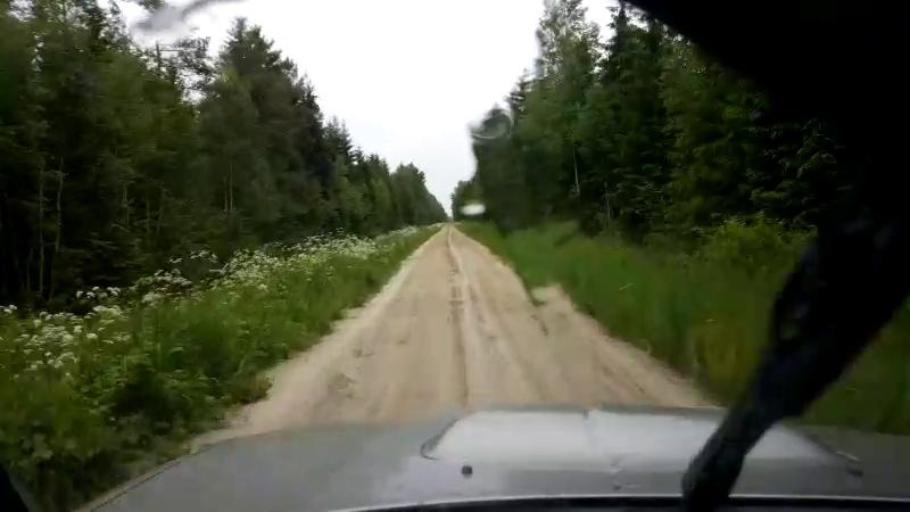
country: EE
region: Paernumaa
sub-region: Halinga vald
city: Parnu-Jaagupi
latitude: 58.5862
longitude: 24.6351
